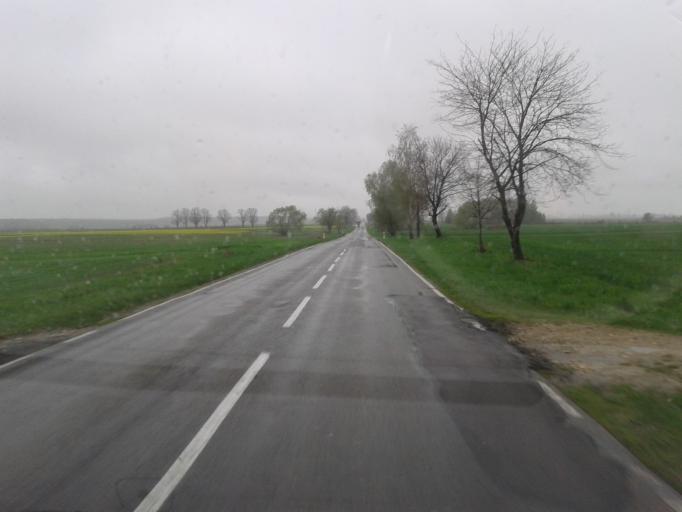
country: PL
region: Subcarpathian Voivodeship
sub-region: Powiat lubaczowski
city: Nowe Siolo
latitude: 50.2891
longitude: 23.1888
